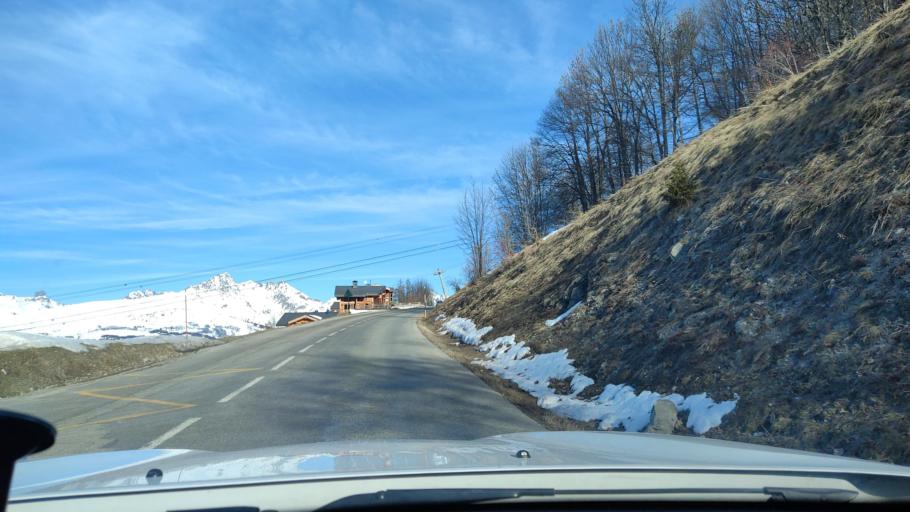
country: FR
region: Rhone-Alpes
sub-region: Departement de la Savoie
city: Belle-Plagne
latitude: 45.5479
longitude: 6.7611
